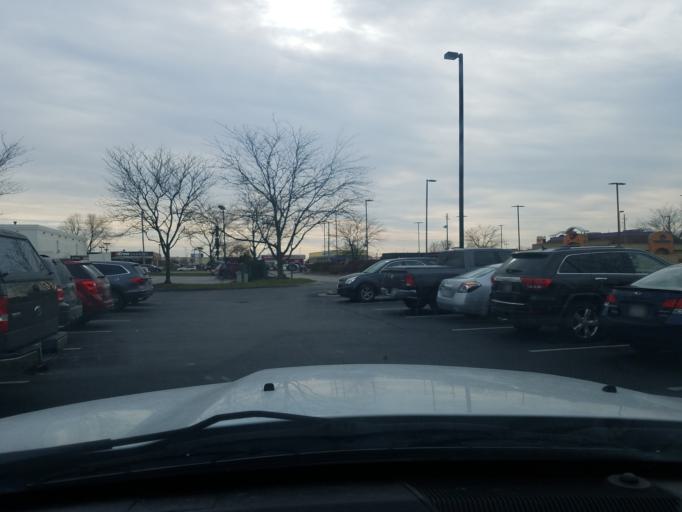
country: US
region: Indiana
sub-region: Hamilton County
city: Fishers
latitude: 39.9282
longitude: -86.0339
